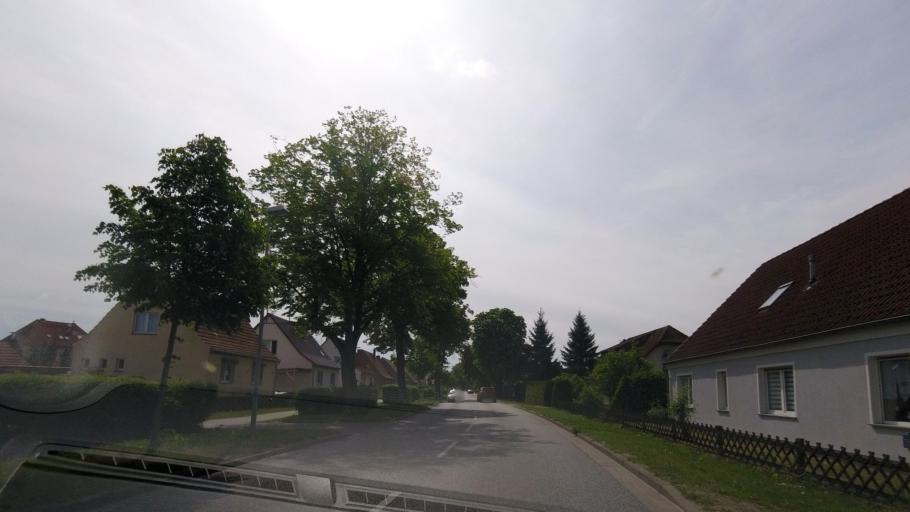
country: DE
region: Brandenburg
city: Wittstock
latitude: 53.1553
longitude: 12.4833
